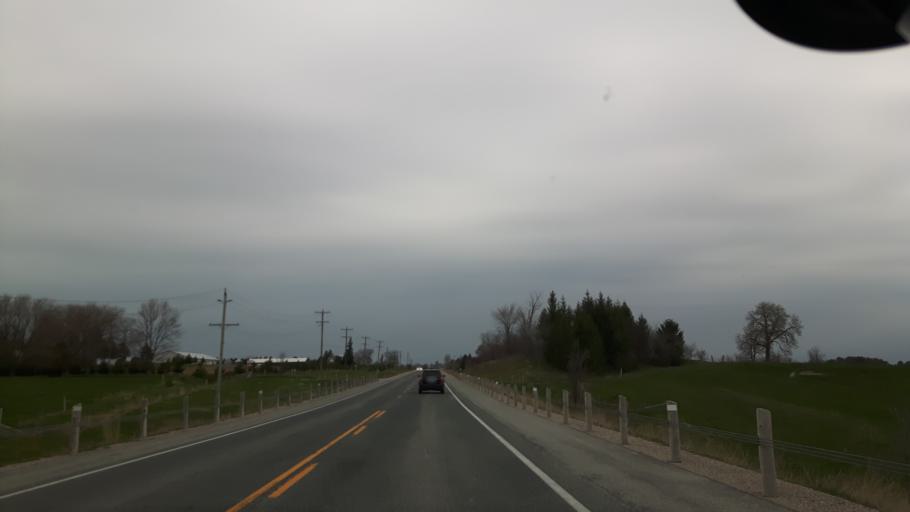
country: CA
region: Ontario
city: Goderich
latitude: 43.6800
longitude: -81.6279
